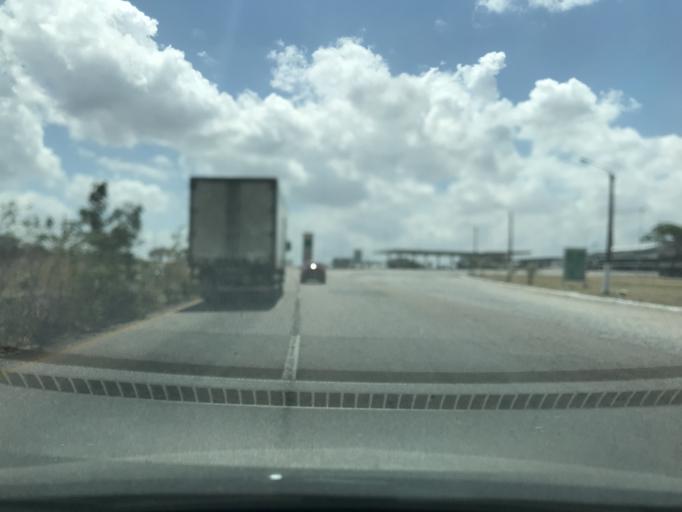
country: BR
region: Pernambuco
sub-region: Caruaru
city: Caruaru
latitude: -8.2942
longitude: -35.8817
